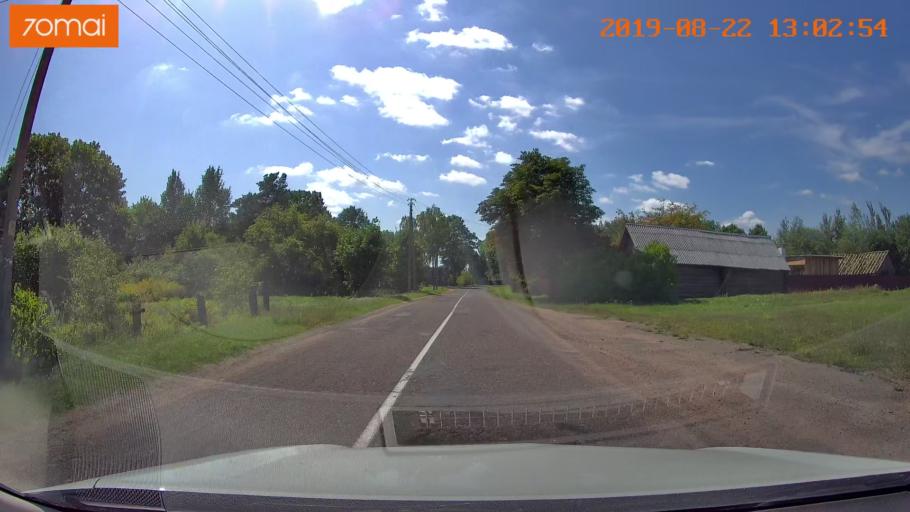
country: BY
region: Minsk
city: Prawdzinski
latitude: 53.3845
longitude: 27.8247
